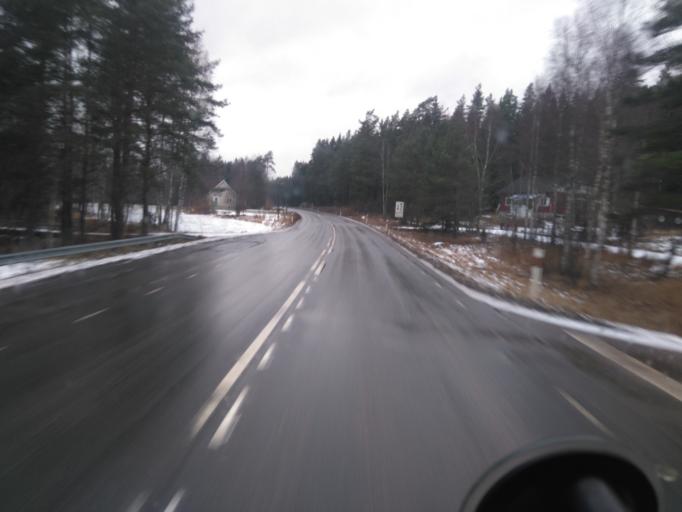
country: SE
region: Joenkoeping
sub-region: Eksjo Kommun
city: Haljarp
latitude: 57.6258
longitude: 15.4474
